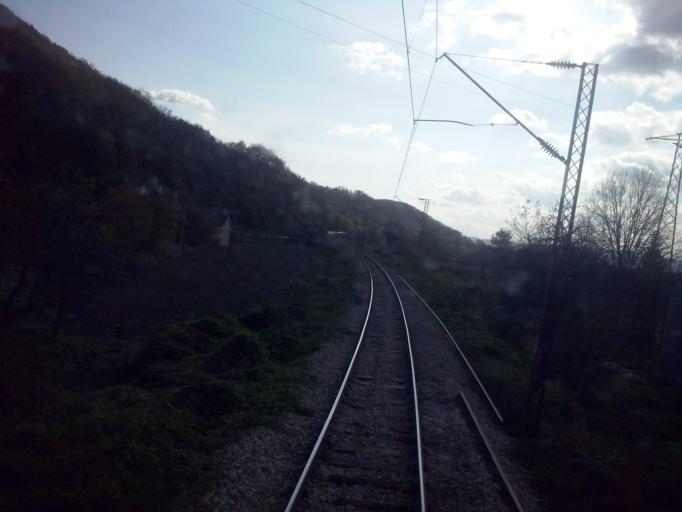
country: RS
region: Central Serbia
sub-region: Zlatiborski Okrug
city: Pozega
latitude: 43.8918
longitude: 19.9962
